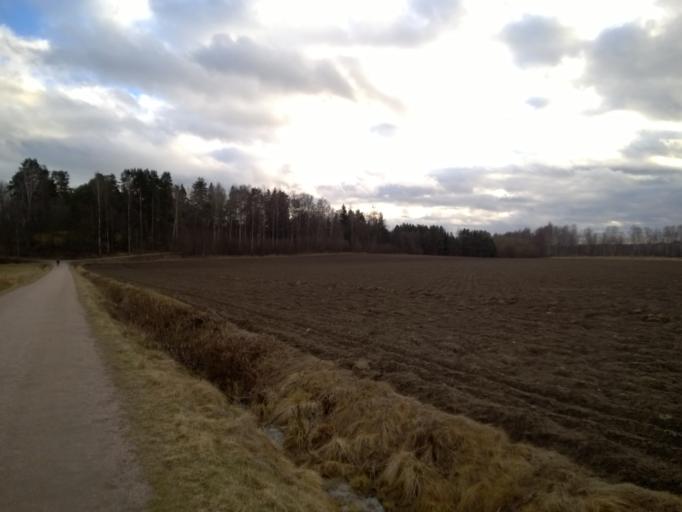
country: FI
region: Uusimaa
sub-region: Helsinki
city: Vantaa
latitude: 60.2228
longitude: 25.0086
